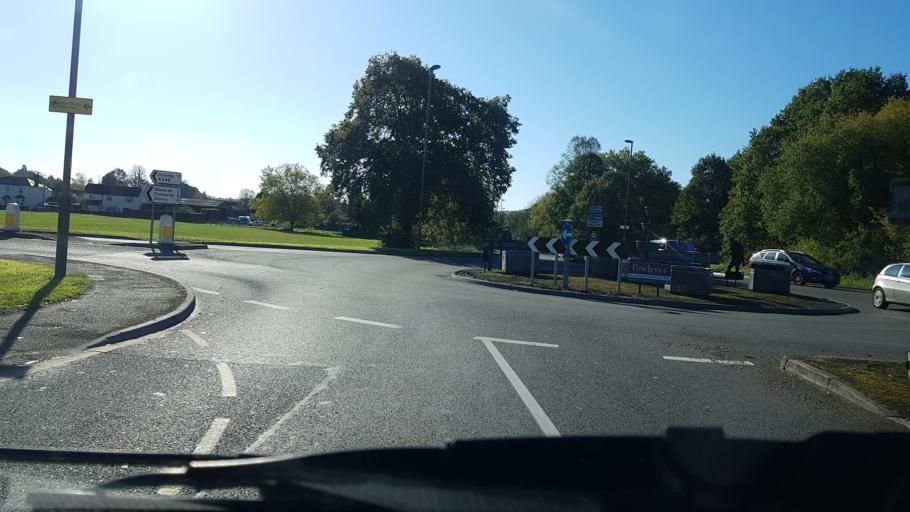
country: GB
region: England
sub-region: Surrey
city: Shalford
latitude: 51.2134
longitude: -0.5682
